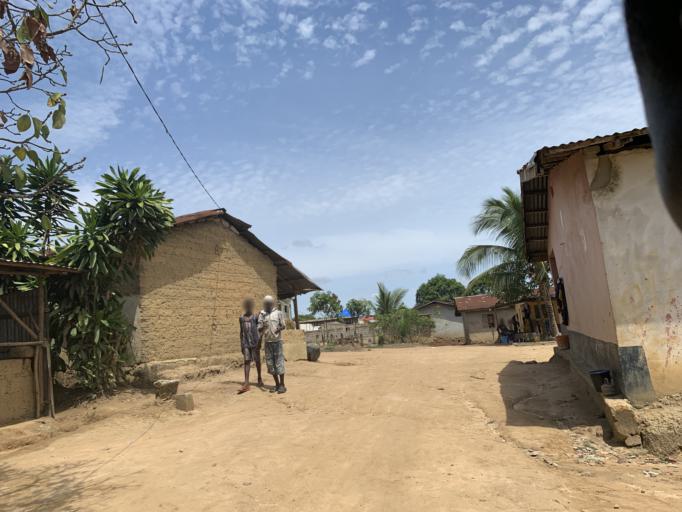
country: SL
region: Western Area
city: Waterloo
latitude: 8.3335
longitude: -13.0464
